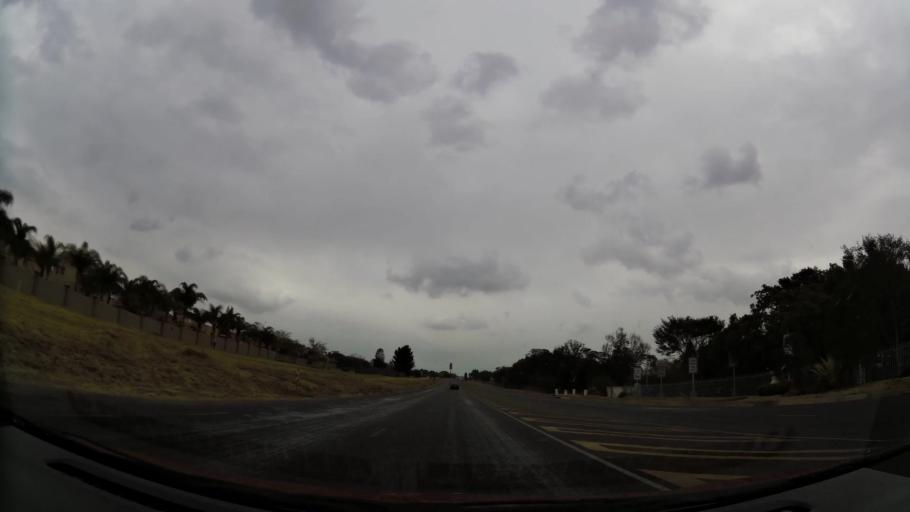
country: ZA
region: Gauteng
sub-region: City of Johannesburg Metropolitan Municipality
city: Roodepoort
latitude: -26.0969
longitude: 27.9267
